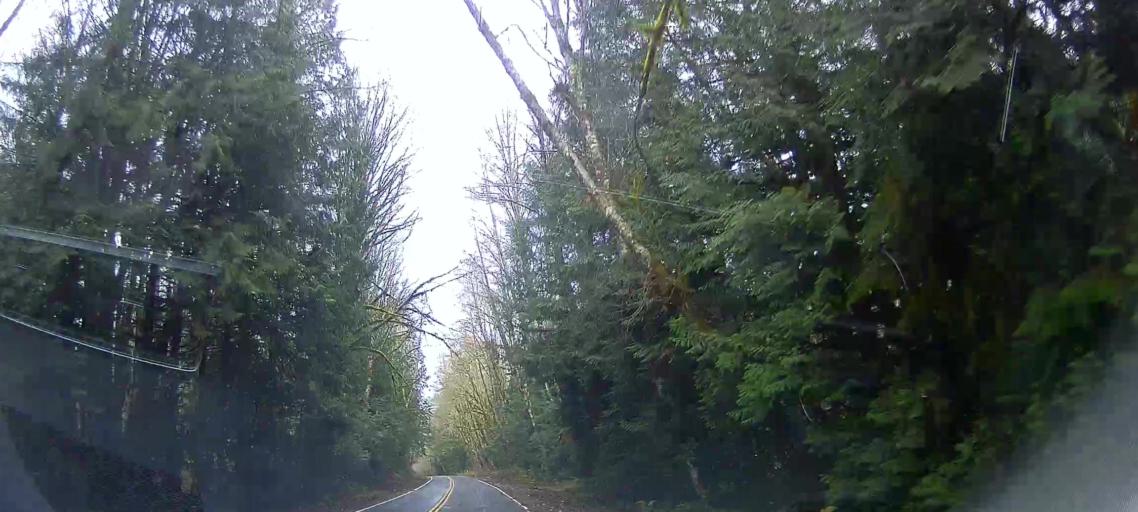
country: US
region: Washington
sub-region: Snohomish County
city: Darrington
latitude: 48.5000
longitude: -121.4623
